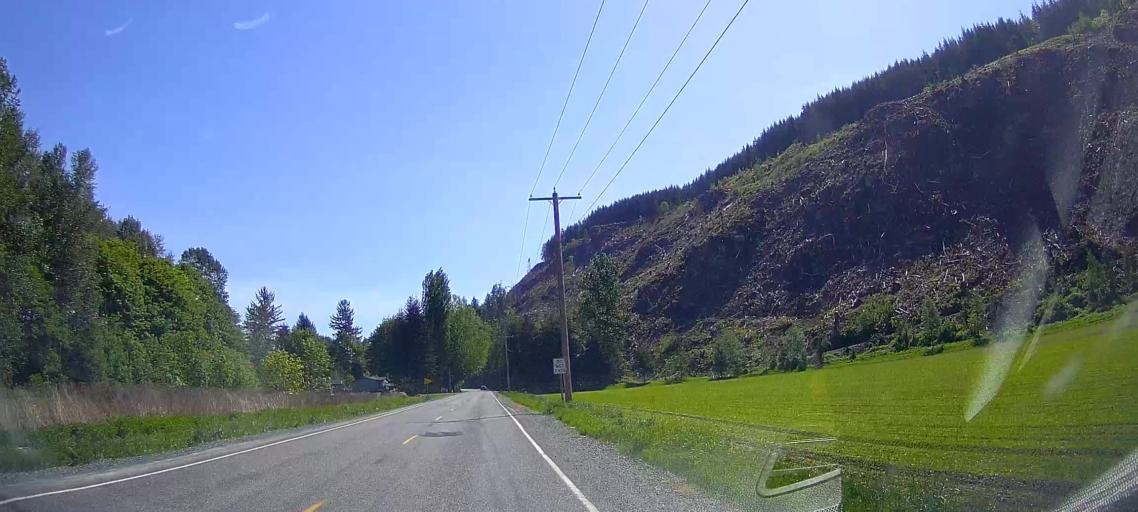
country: US
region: Washington
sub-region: Skagit County
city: Sedro-Woolley
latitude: 48.4869
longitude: -122.2225
